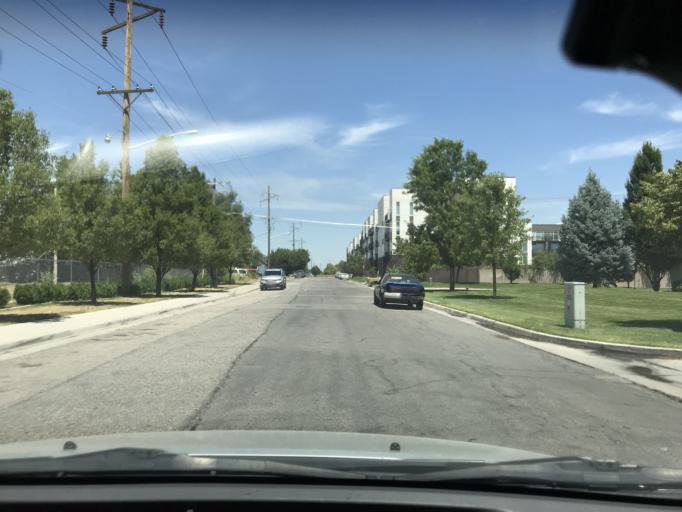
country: US
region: Utah
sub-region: Salt Lake County
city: Salt Lake City
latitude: 40.7689
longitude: -111.9439
